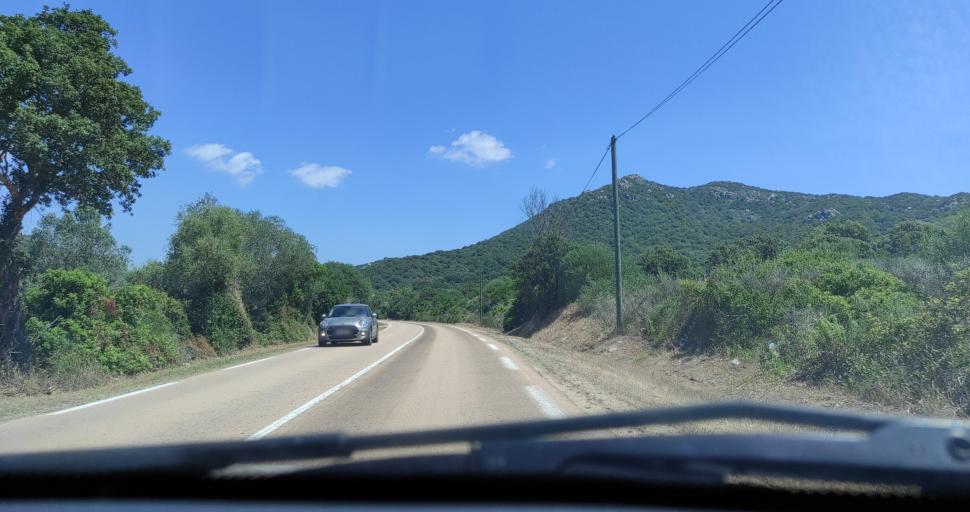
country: FR
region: Corsica
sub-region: Departement de la Corse-du-Sud
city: Bonifacio
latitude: 41.5073
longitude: 9.1469
